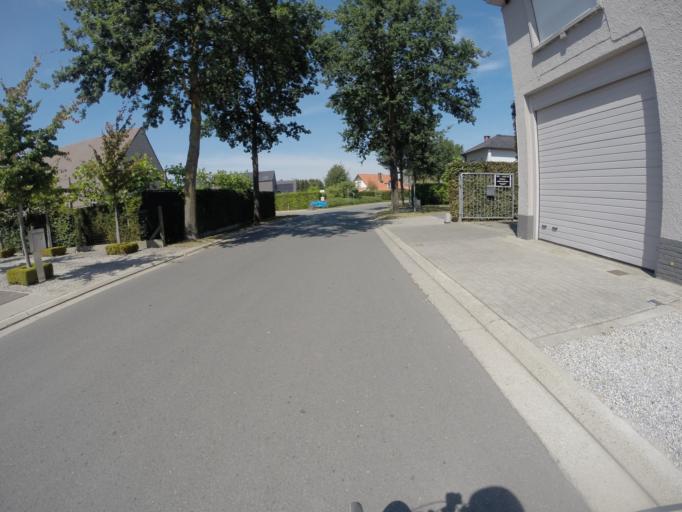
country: BE
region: Flanders
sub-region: Provincie Oost-Vlaanderen
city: Knesselare
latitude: 51.1410
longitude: 3.4154
